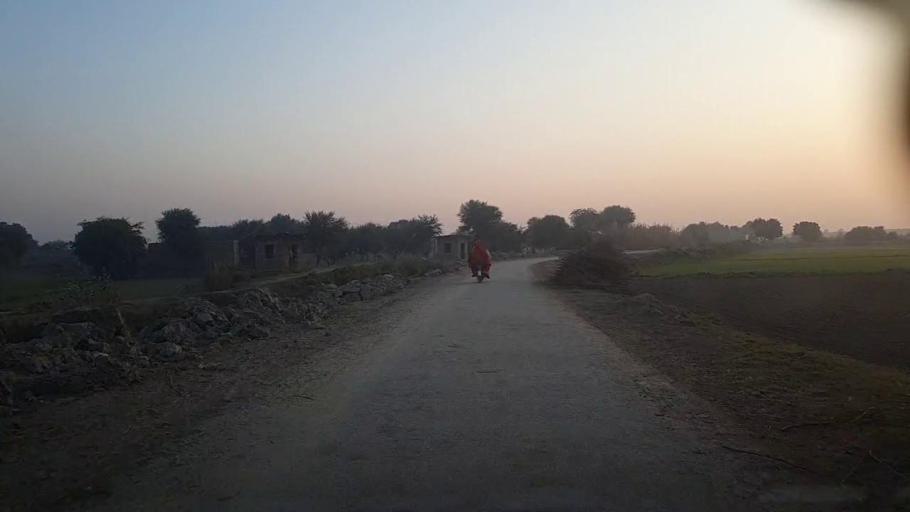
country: PK
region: Sindh
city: Karaundi
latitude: 26.8362
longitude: 68.3691
